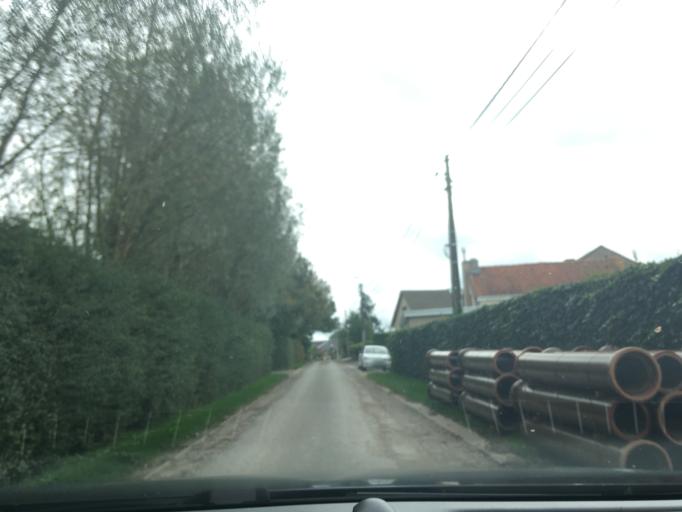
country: BE
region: Flanders
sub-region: Provincie West-Vlaanderen
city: Moorslede
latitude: 50.9030
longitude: 3.0623
